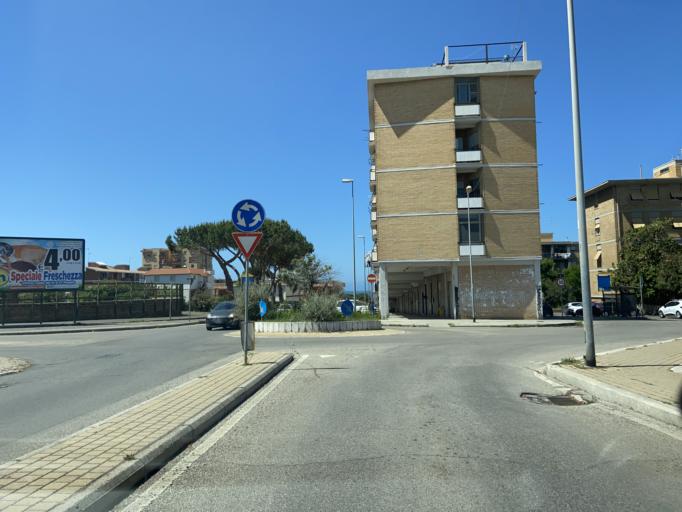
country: IT
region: Latium
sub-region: Citta metropolitana di Roma Capitale
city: Civitavecchia
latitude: 42.0832
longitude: 11.8131
